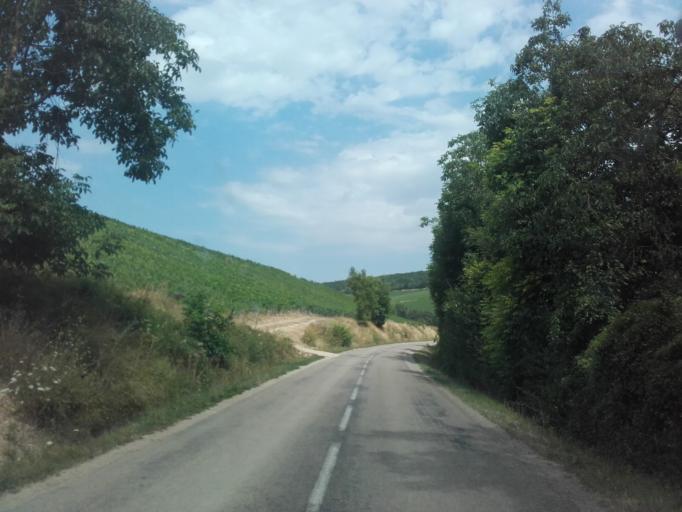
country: FR
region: Bourgogne
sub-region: Departement de l'Yonne
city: Chablis
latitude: 47.8171
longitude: 3.8134
